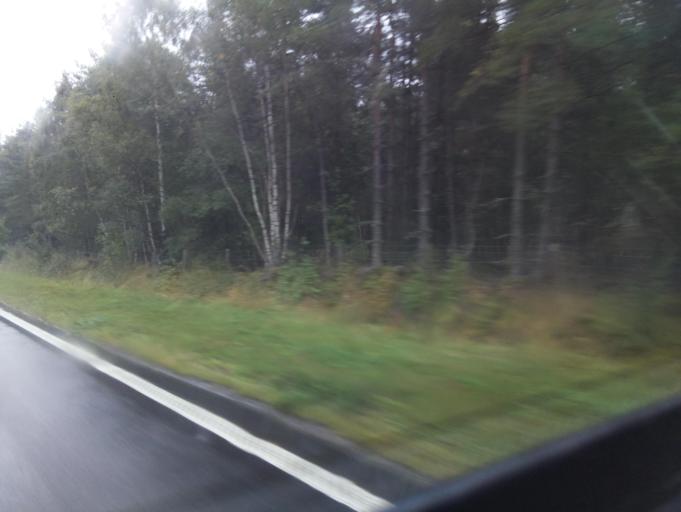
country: GB
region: Scotland
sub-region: Highland
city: Grantown on Spey
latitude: 57.2820
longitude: -3.6959
